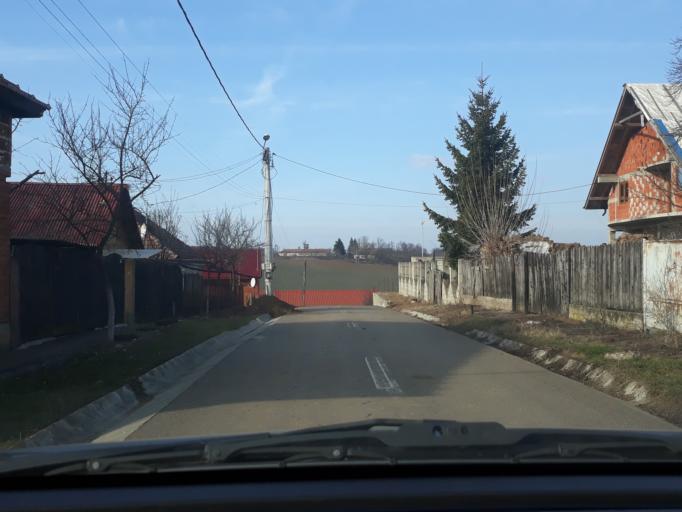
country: RO
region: Bihor
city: Margita
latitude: 47.3610
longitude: 22.3301
